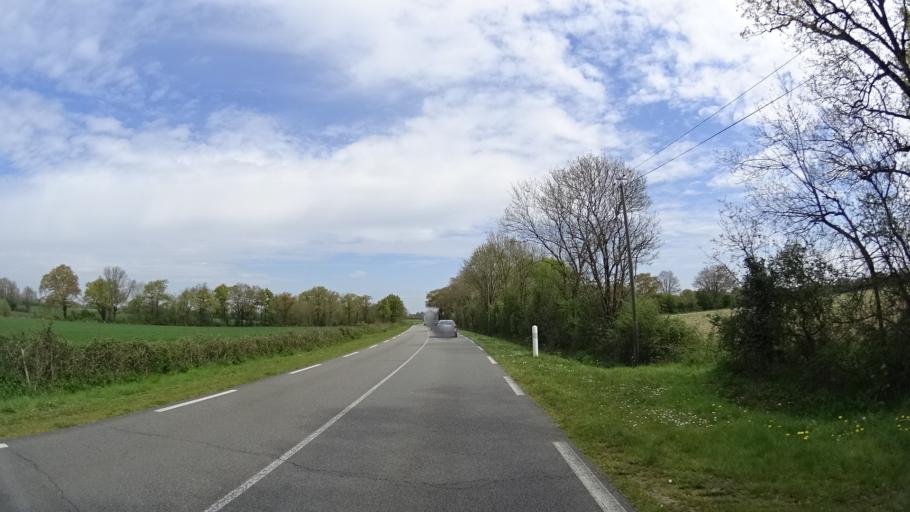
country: FR
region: Pays de la Loire
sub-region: Departement de la Loire-Atlantique
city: Saint-Hilaire-de-Chaleons
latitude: 47.0867
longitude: -1.8465
